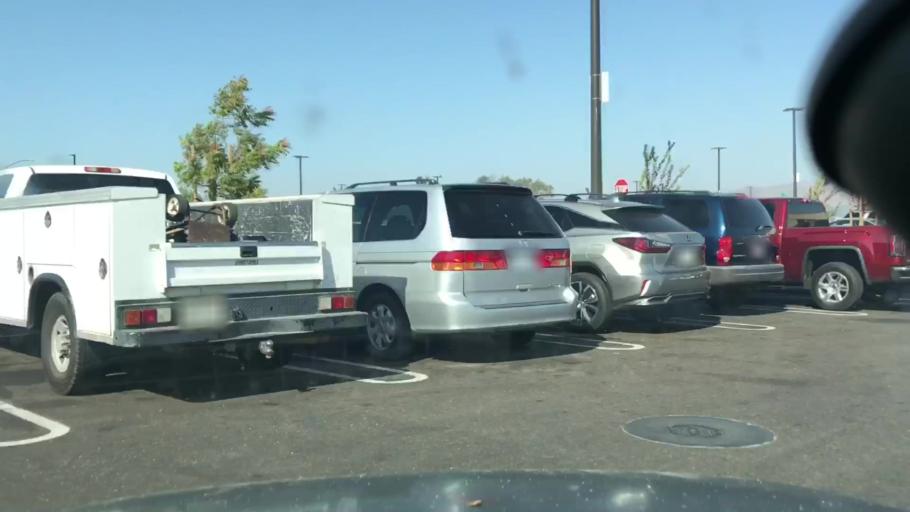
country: US
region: California
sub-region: Santa Barbara County
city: Santa Maria
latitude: 34.9269
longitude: -120.4204
